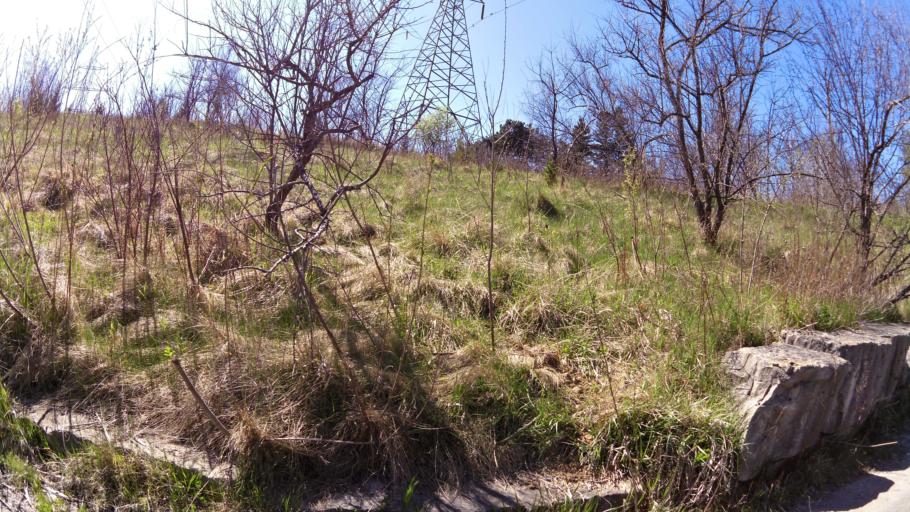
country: CA
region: Ontario
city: Concord
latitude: 43.7626
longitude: -79.5092
